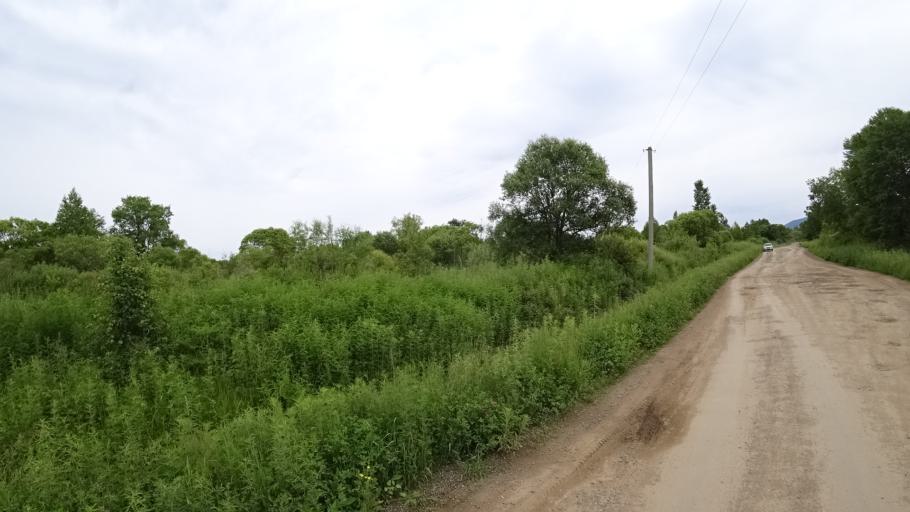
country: RU
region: Primorskiy
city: Arsen'yev
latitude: 44.1953
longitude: 133.3087
